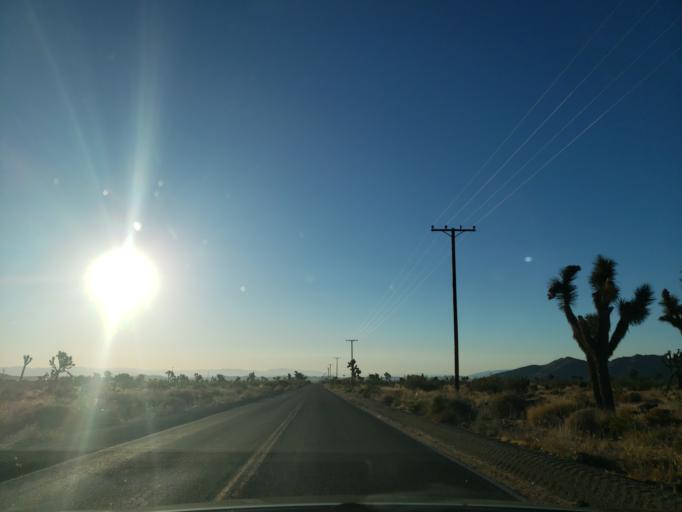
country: US
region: California
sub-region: San Bernardino County
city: Joshua Tree
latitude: 34.1930
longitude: -116.3798
